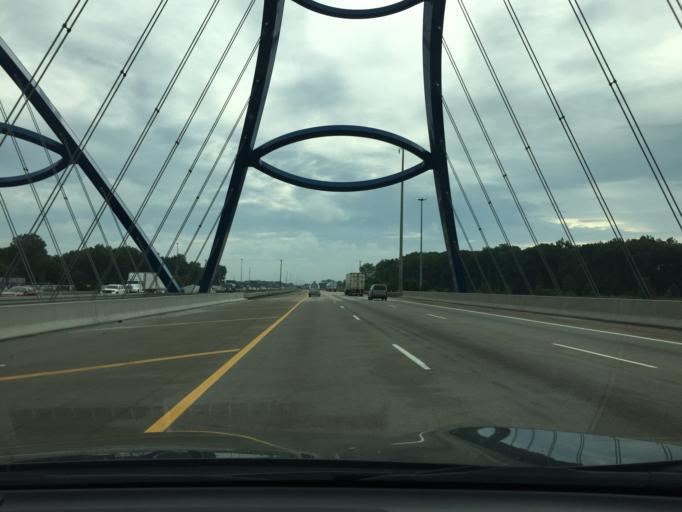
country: US
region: Michigan
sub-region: Wayne County
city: Taylor
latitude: 42.2647
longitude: -83.2709
